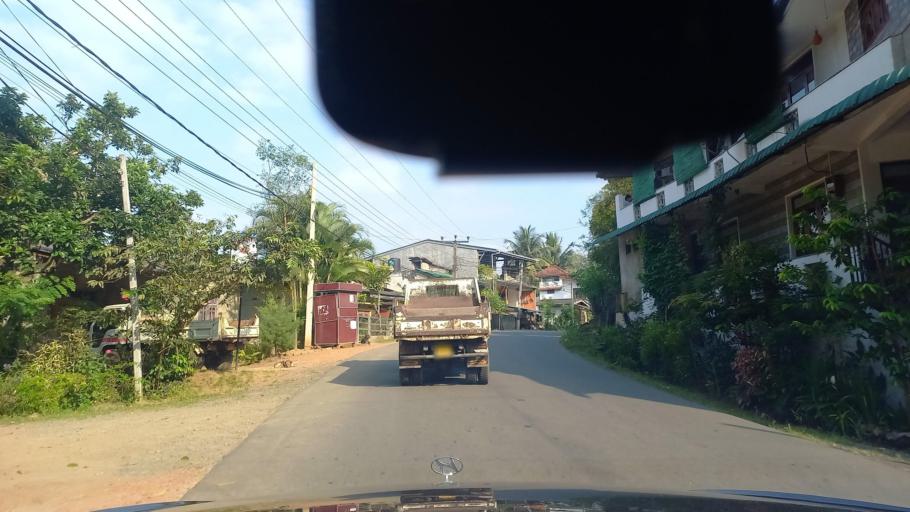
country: LK
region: Central
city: Kandy
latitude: 7.2319
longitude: 80.6031
